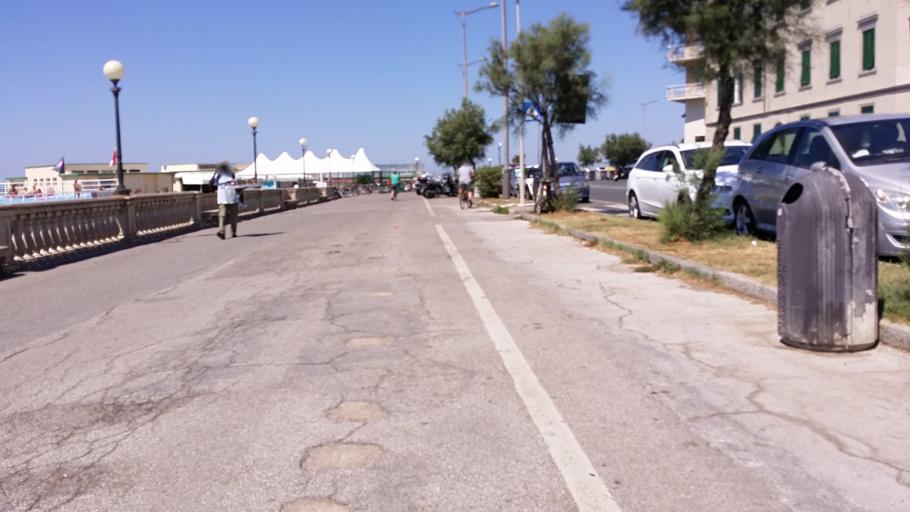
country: IT
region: Tuscany
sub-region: Provincia di Livorno
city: Livorno
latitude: 43.5304
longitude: 10.3046
